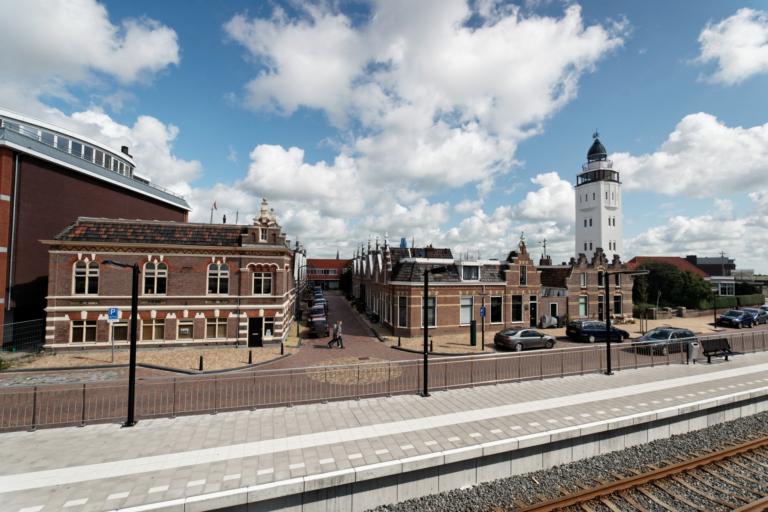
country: NL
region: Friesland
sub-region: Gemeente Harlingen
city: Harlingen
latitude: 53.1743
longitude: 5.4114
